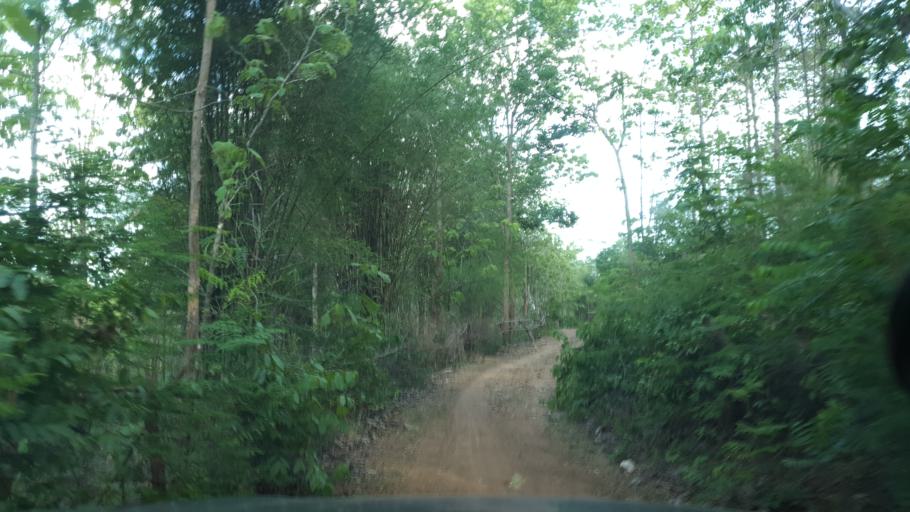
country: TH
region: Lampang
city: Sop Prap
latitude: 17.8909
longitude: 99.2869
